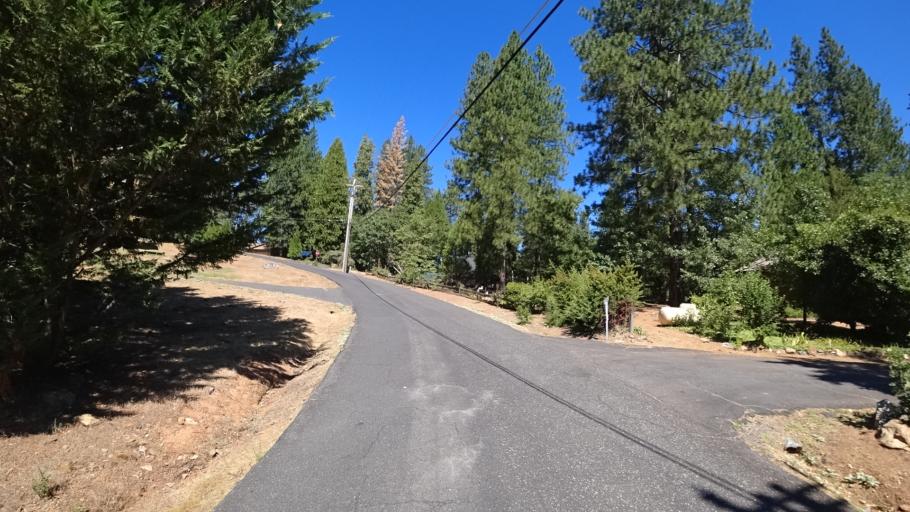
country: US
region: California
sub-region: Calaveras County
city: Forest Meadows
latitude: 38.1866
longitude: -120.3661
